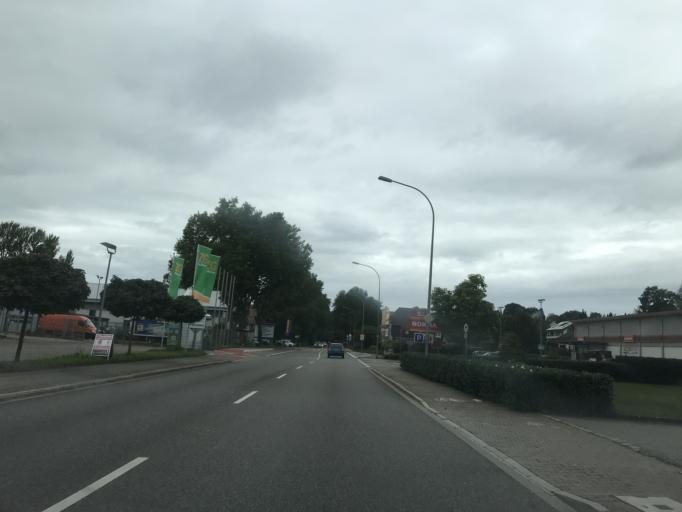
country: DE
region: Baden-Wuerttemberg
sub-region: Freiburg Region
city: Bad Sackingen
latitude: 47.5605
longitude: 7.9618
